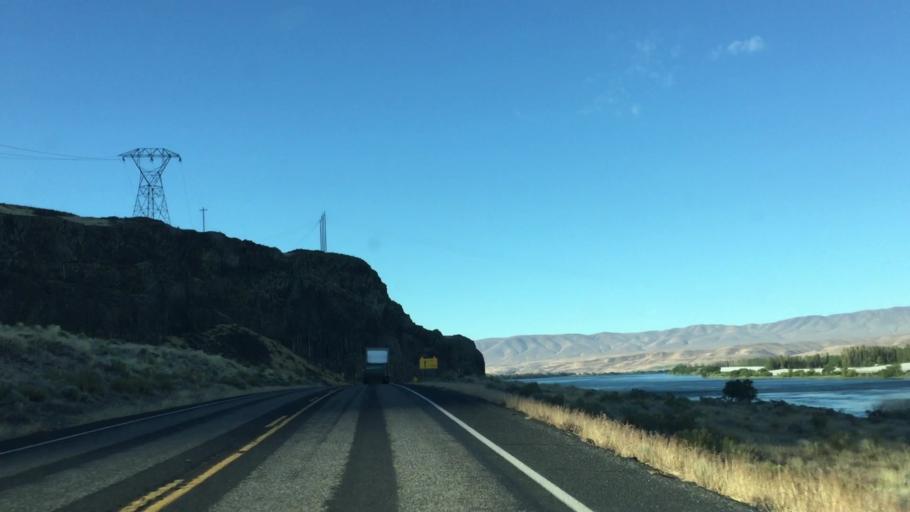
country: US
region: Washington
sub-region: Grant County
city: Mattawa
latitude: 46.8037
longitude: -119.9226
